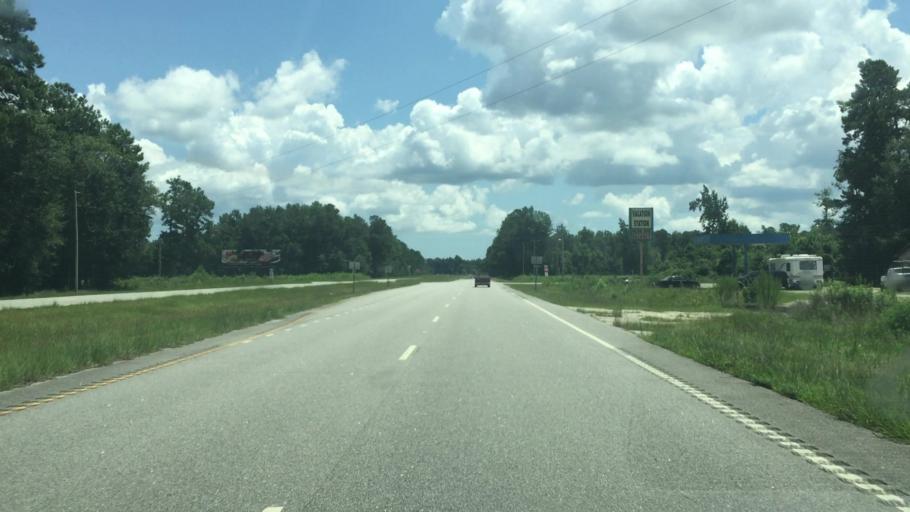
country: US
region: South Carolina
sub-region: Horry County
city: Loris
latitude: 34.0262
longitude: -78.7999
